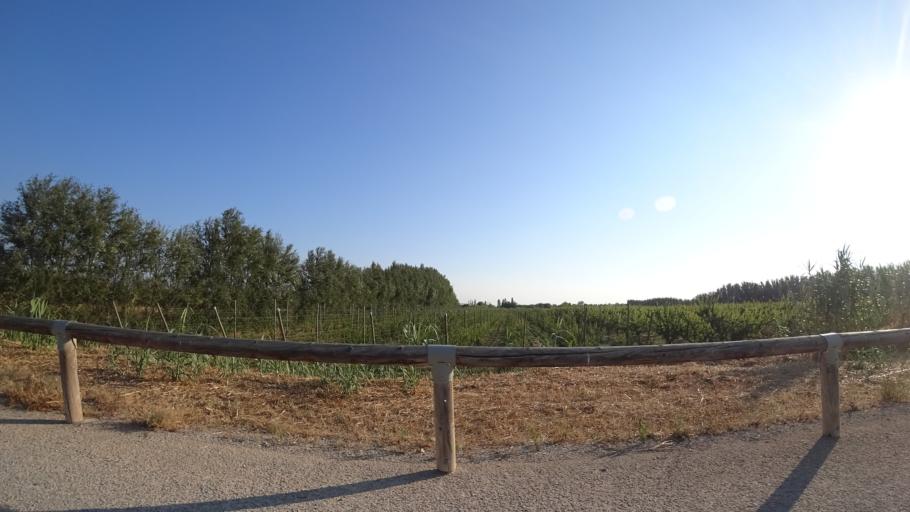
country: FR
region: Languedoc-Roussillon
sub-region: Departement des Pyrenees-Orientales
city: Pia
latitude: 42.7616
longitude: 2.9169
